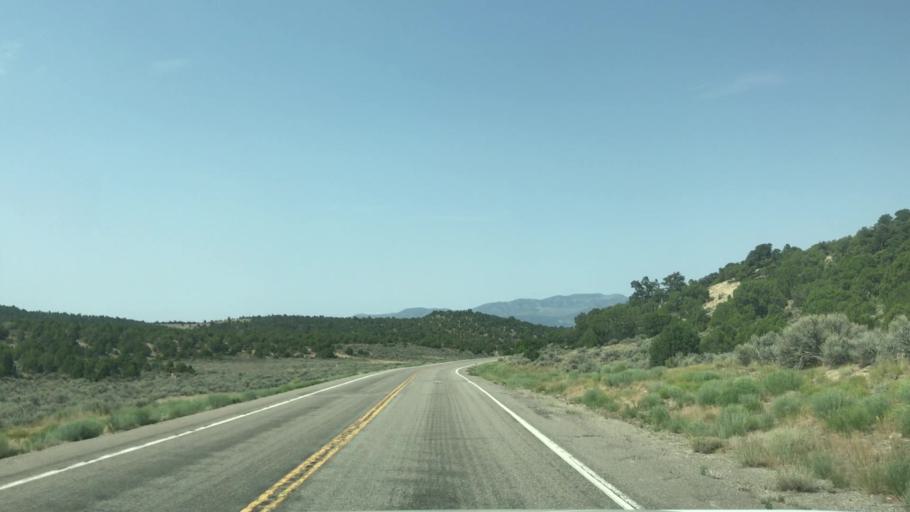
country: US
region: Nevada
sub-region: White Pine County
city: Ely
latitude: 39.0248
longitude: -114.6715
